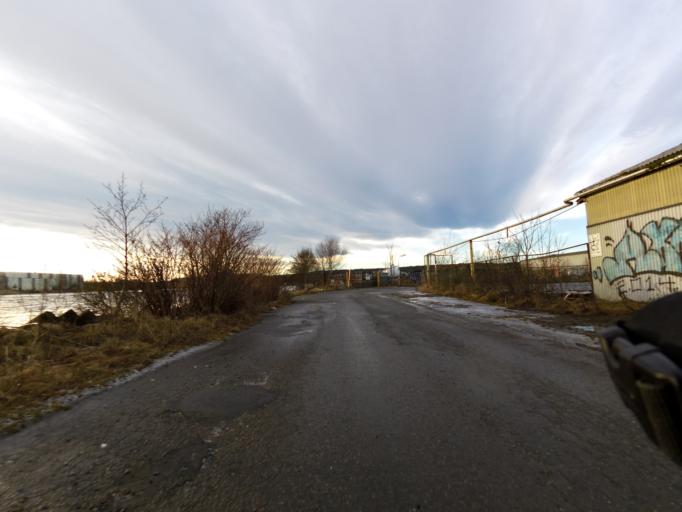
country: NO
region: Ostfold
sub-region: Fredrikstad
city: Fredrikstad
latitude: 59.2152
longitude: 10.9227
